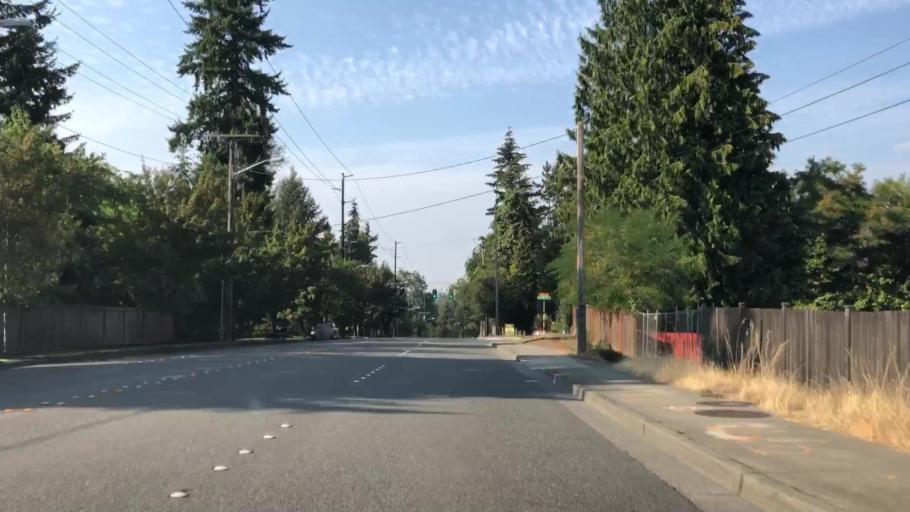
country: US
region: Washington
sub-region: King County
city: Clyde Hill
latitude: 47.6361
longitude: -122.2016
